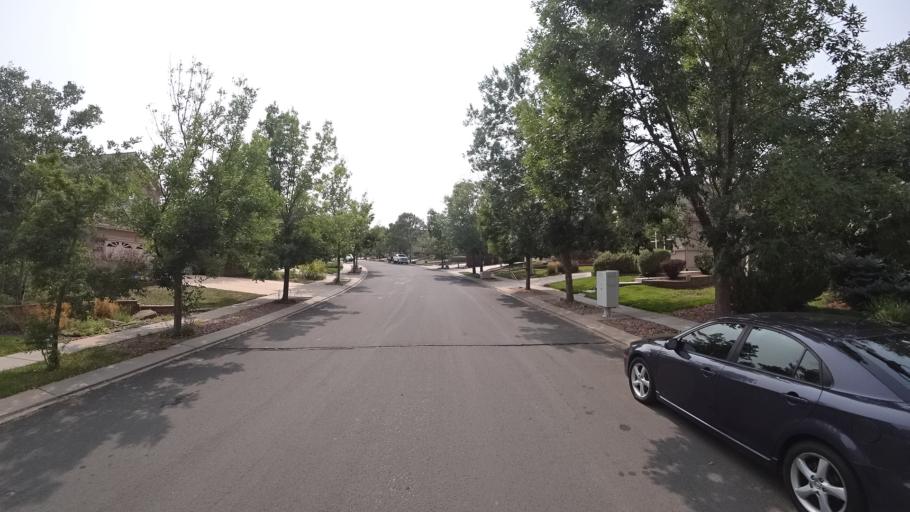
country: US
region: Colorado
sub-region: El Paso County
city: Cimarron Hills
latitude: 38.9250
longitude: -104.7472
